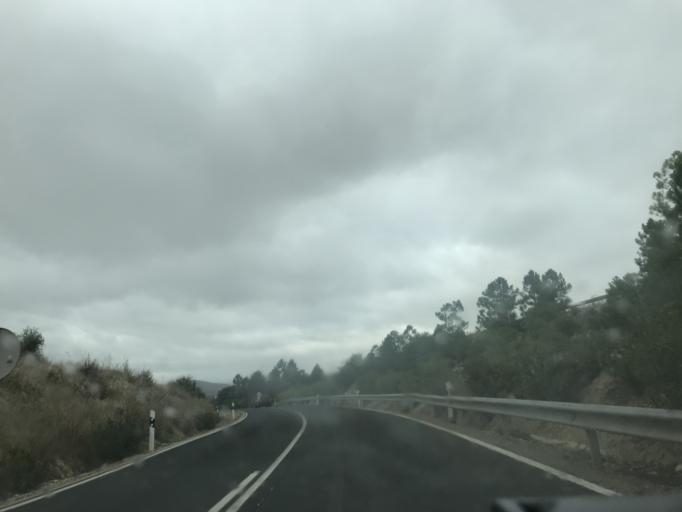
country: ES
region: Andalusia
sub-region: Provincia de Jaen
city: Peal de Becerro
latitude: 37.9176
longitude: -3.1085
